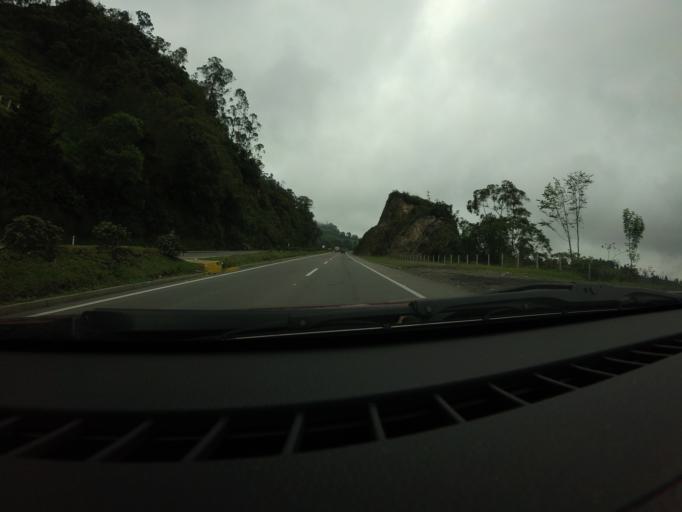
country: CO
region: Cundinamarca
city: San Francisco
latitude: 4.9474
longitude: -74.3042
